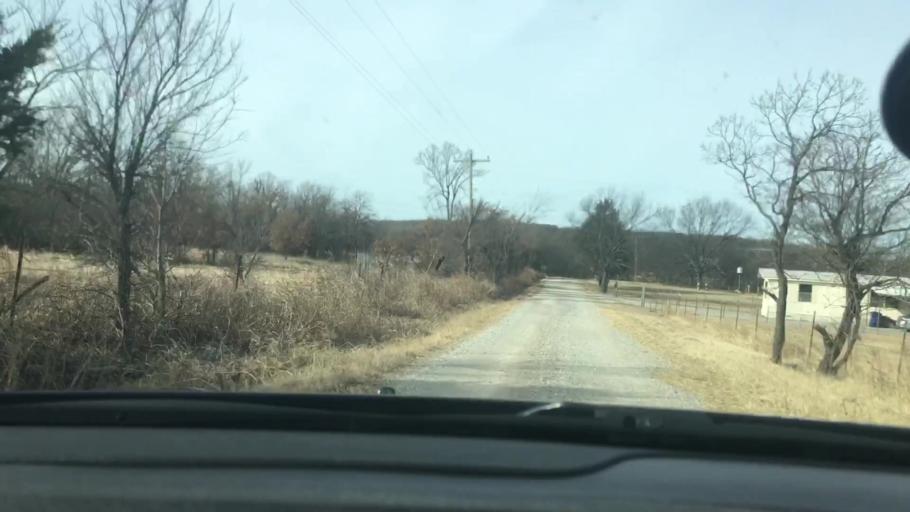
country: US
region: Oklahoma
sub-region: Garvin County
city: Wynnewood
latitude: 34.6374
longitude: -97.2457
